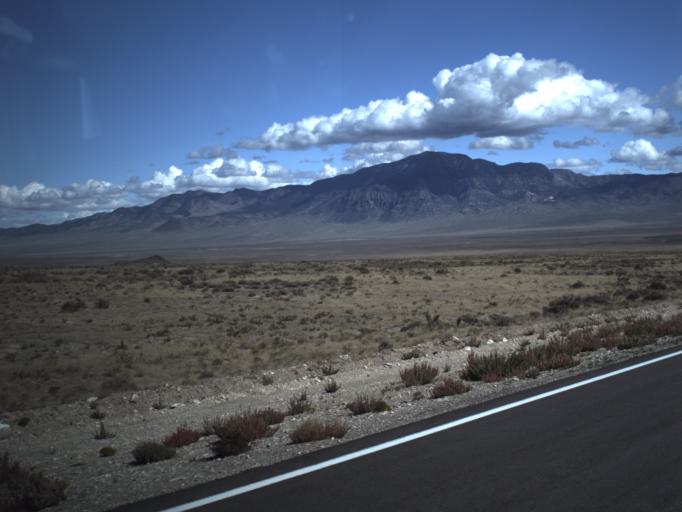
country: US
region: Utah
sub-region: Beaver County
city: Milford
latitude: 38.4951
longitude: -113.4827
